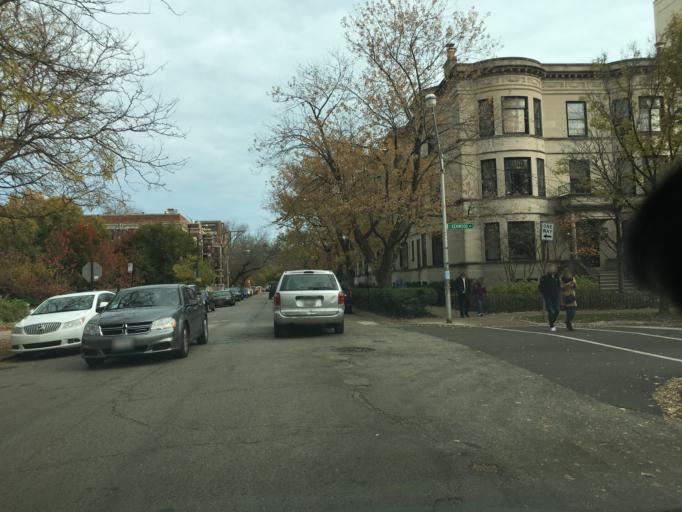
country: US
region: Illinois
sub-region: Cook County
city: Chicago
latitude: 41.7915
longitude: -87.5935
